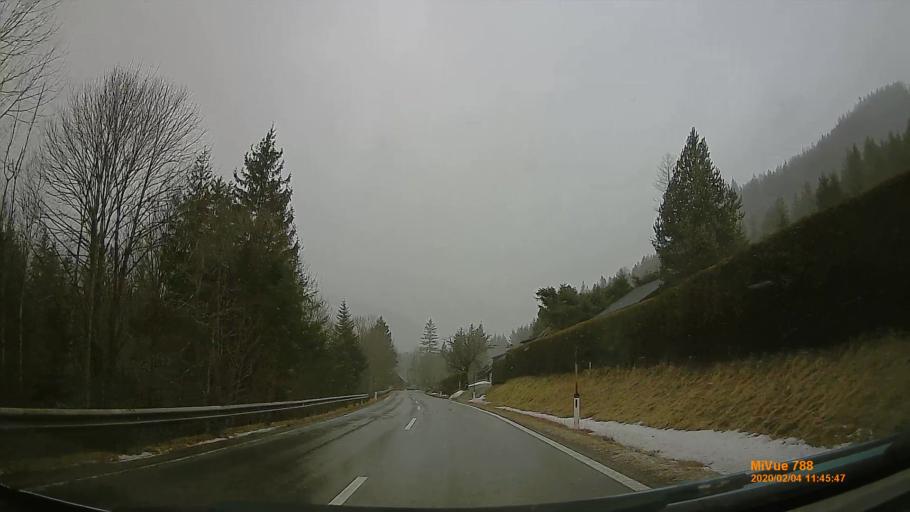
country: AT
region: Styria
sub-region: Politischer Bezirk Bruck-Muerzzuschlag
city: Muerzsteg
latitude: 47.6960
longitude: 15.4815
